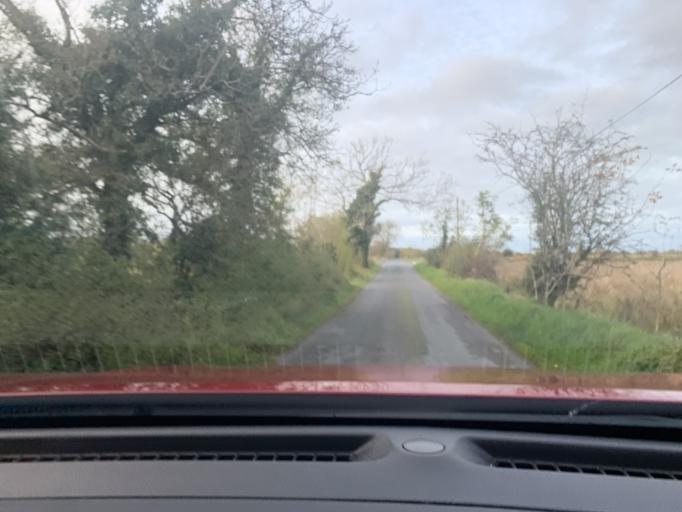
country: IE
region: Connaught
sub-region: Roscommon
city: Ballaghaderreen
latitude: 54.0001
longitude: -8.6068
